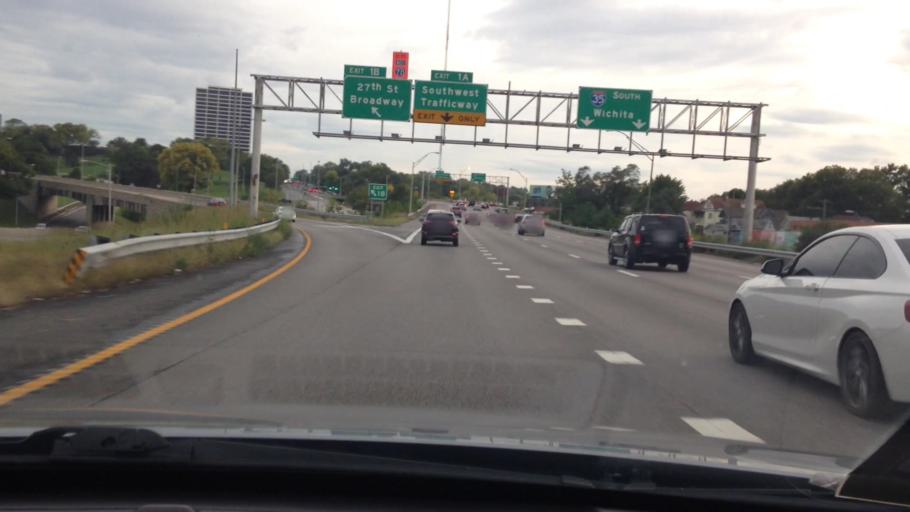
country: US
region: Missouri
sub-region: Jackson County
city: Kansas City
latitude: 39.0816
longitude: -94.5935
